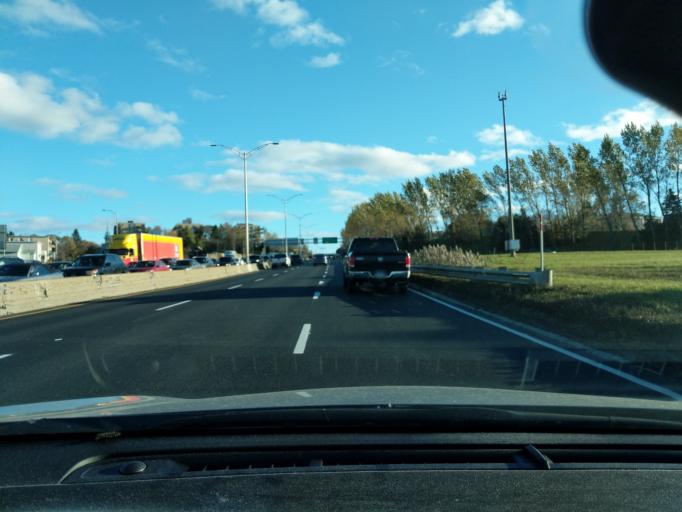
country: CA
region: Quebec
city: L'Ancienne-Lorette
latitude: 46.7819
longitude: -71.3095
